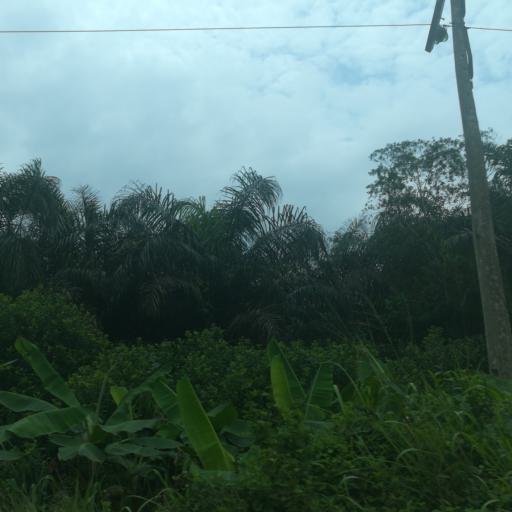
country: NG
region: Lagos
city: Ejirin
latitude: 6.6511
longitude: 3.7907
